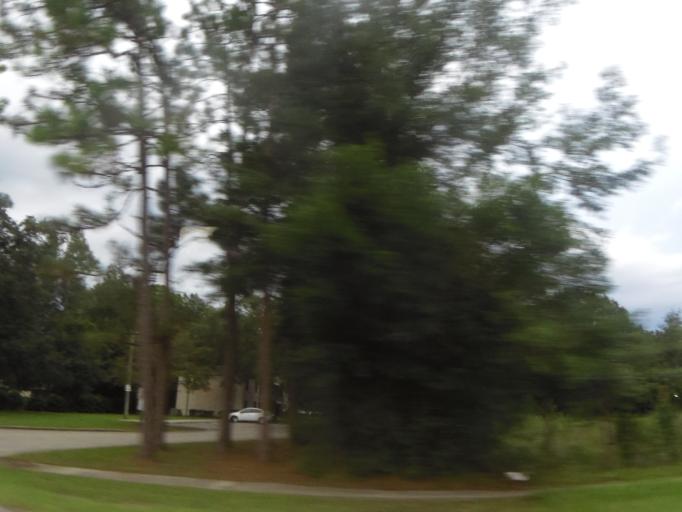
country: US
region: Florida
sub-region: Clay County
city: Bellair-Meadowbrook Terrace
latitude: 30.2843
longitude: -81.7916
